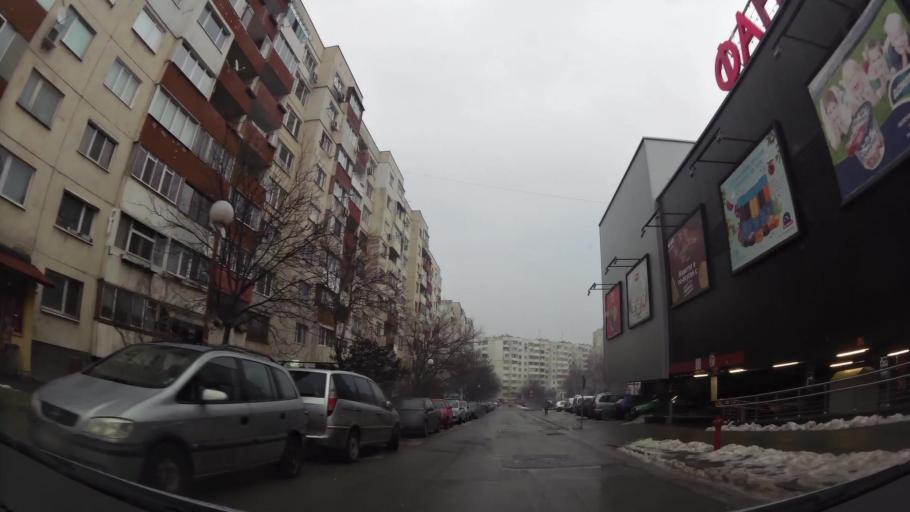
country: BG
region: Sofia-Capital
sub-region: Stolichna Obshtina
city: Sofia
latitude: 42.6864
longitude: 23.2557
